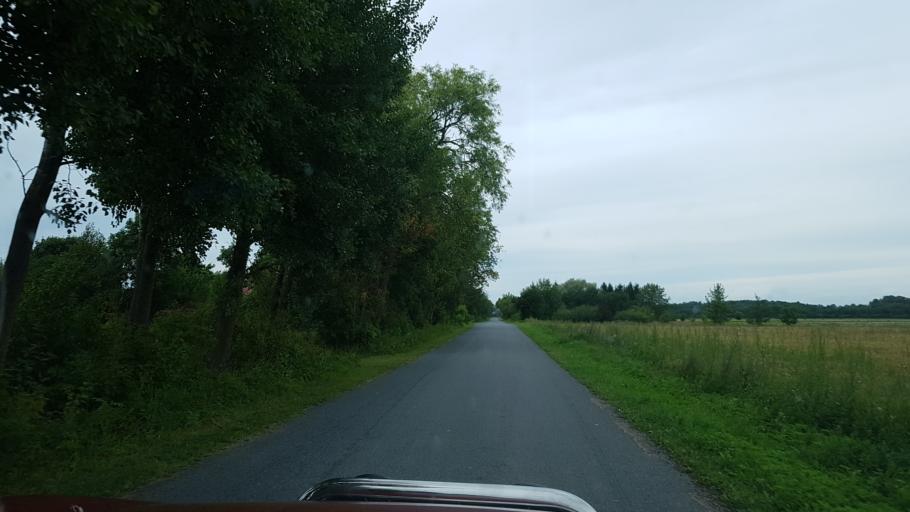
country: EE
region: Laeaene
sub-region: Ridala Parish
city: Uuemoisa
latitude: 58.7922
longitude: 23.6618
